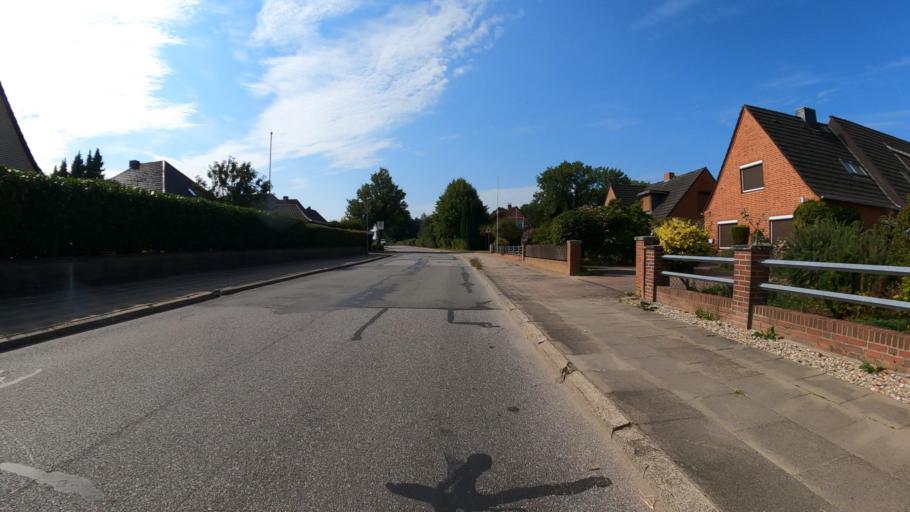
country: DE
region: Schleswig-Holstein
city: Hamwarde
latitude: 53.4486
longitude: 10.4196
